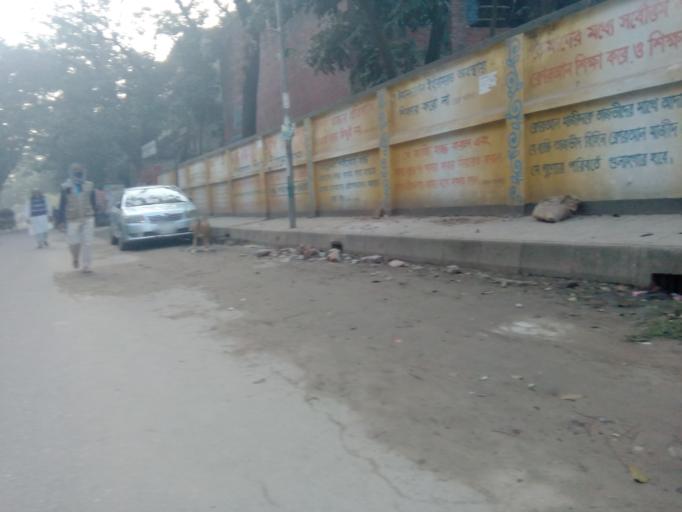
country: BD
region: Dhaka
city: Paltan
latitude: 23.7508
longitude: 90.4217
